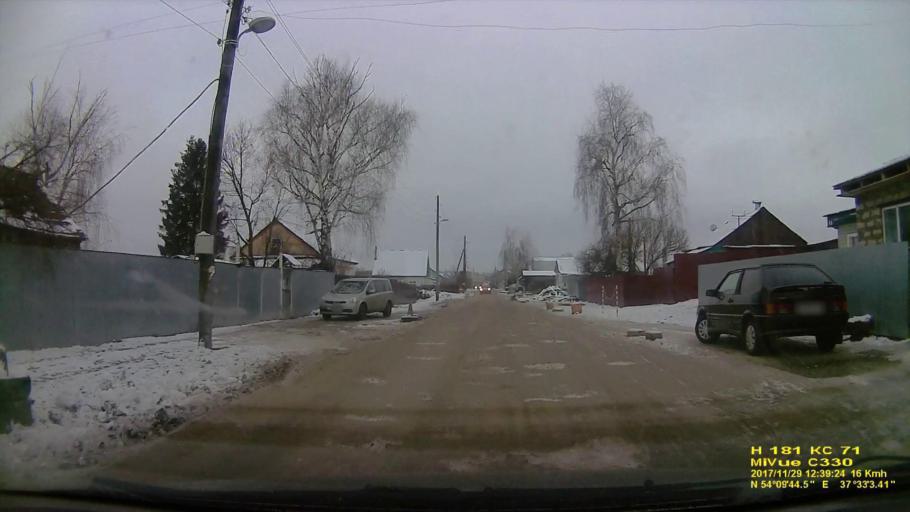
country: RU
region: Tula
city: Kosaya Gora
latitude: 54.1624
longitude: 37.5509
